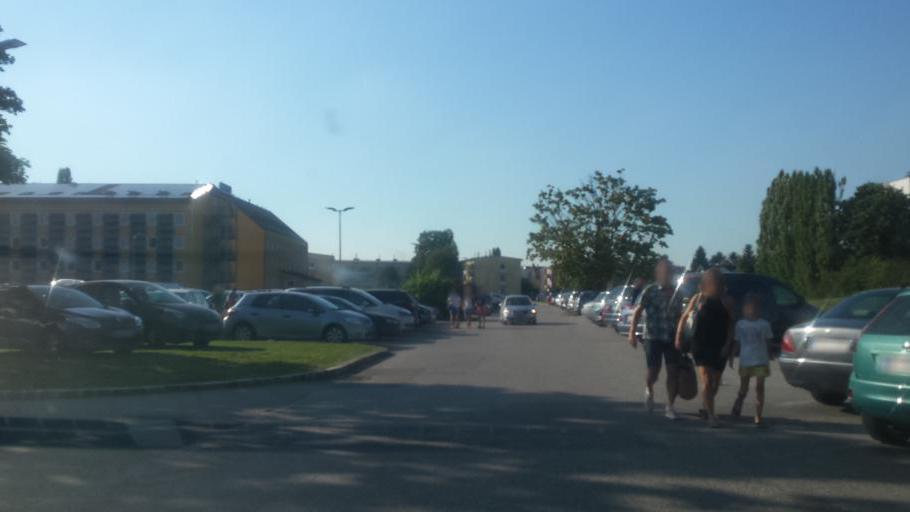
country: AT
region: Lower Austria
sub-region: Politischer Bezirk Korneuburg
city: Bisamberg
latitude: 48.3369
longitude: 16.3436
